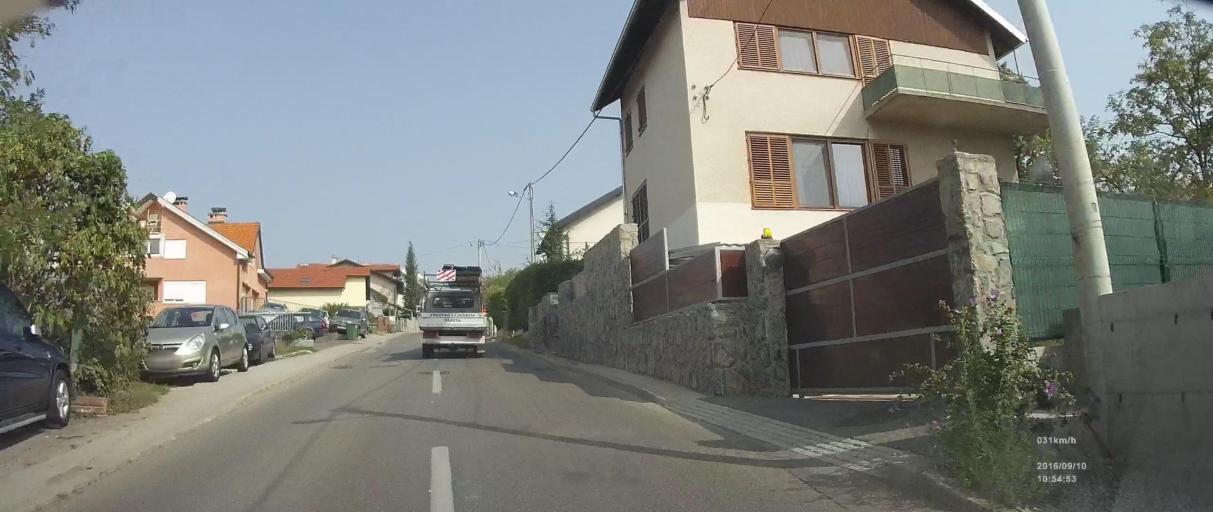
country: HR
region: Grad Zagreb
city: Zagreb
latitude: 45.8285
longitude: 15.9385
